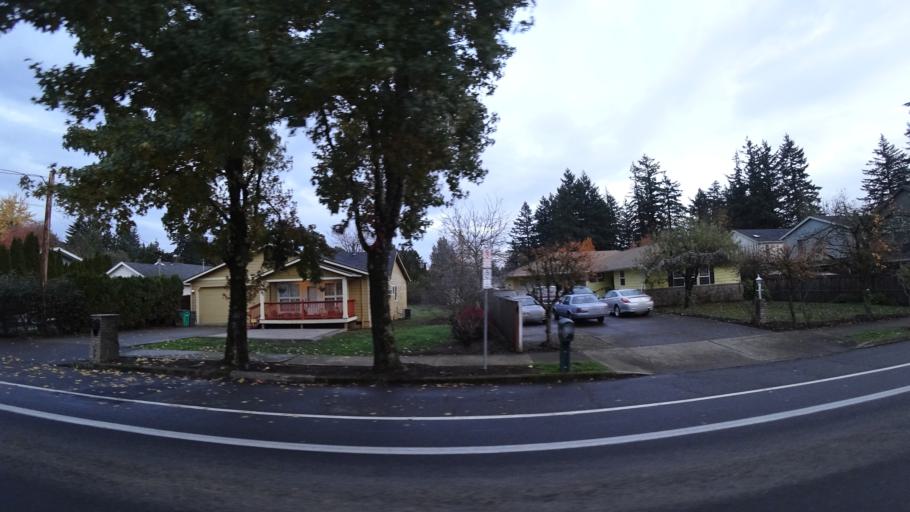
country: US
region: Oregon
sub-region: Multnomah County
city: Lents
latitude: 45.5239
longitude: -122.5106
